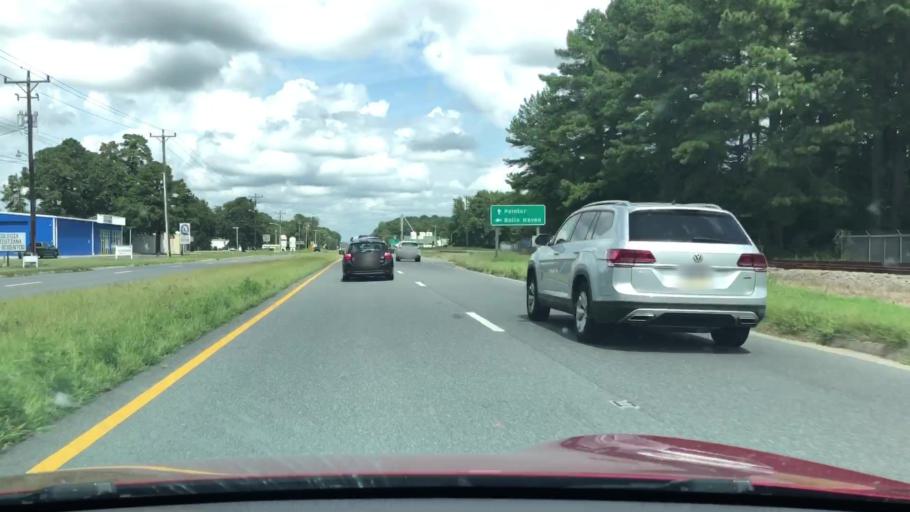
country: US
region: Virginia
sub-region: Northampton County
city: Exmore
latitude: 37.5485
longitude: -75.8133
